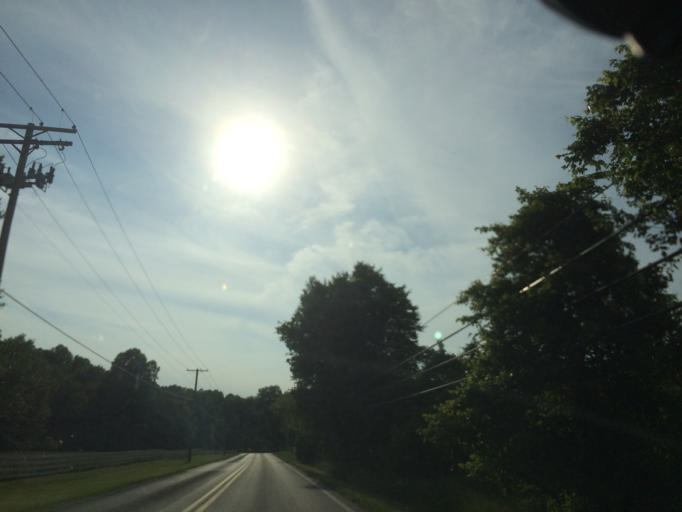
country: US
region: Maryland
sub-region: Howard County
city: Highland
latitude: 39.2567
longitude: -76.9630
